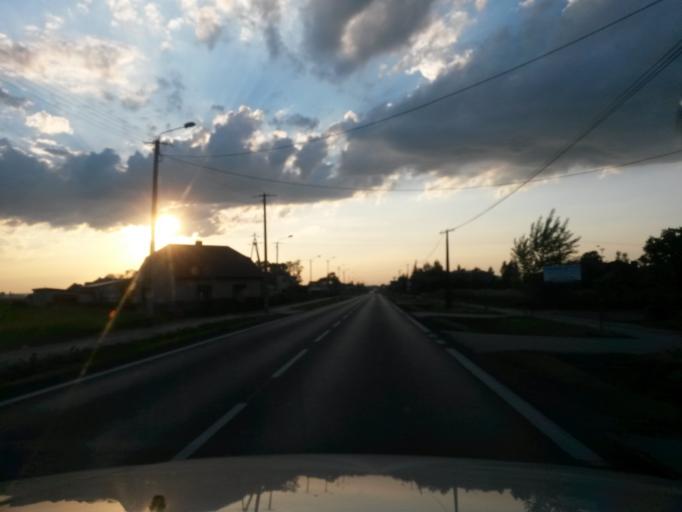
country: PL
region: Lodz Voivodeship
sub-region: Powiat wielunski
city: Wielun
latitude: 51.2327
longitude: 18.5395
